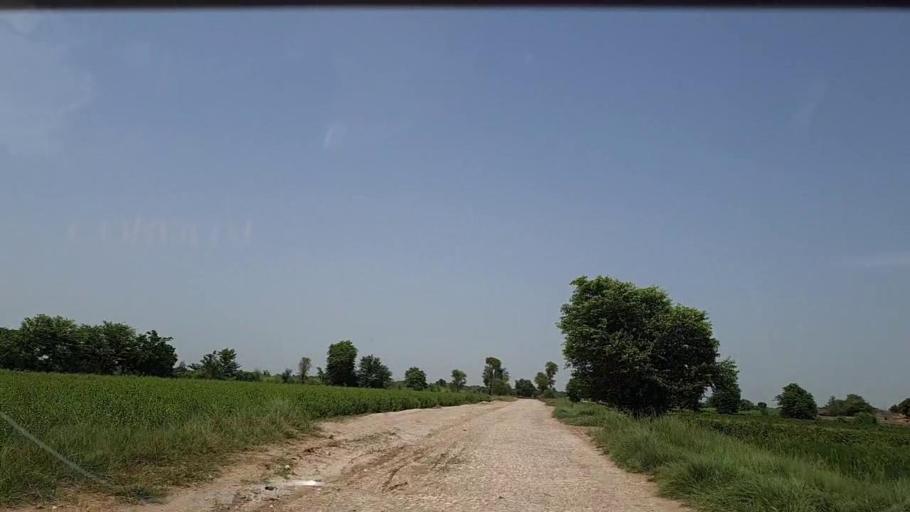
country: PK
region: Sindh
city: Tharu Shah
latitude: 26.9536
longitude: 68.0434
